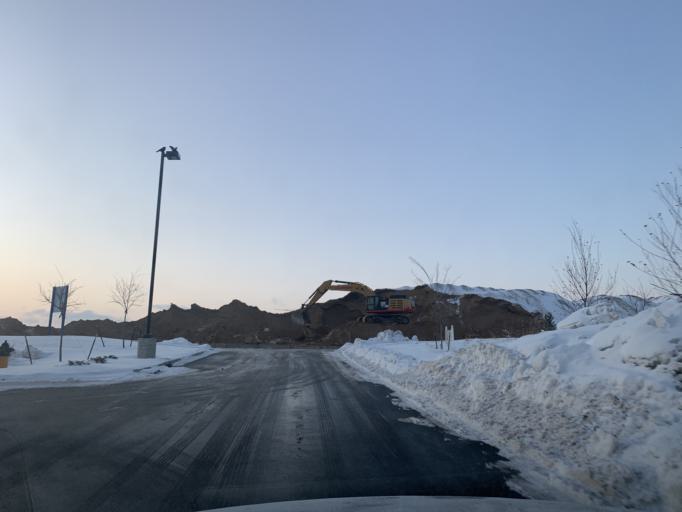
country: US
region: Minnesota
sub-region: Scott County
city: Shakopee
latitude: 44.7941
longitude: -93.4880
